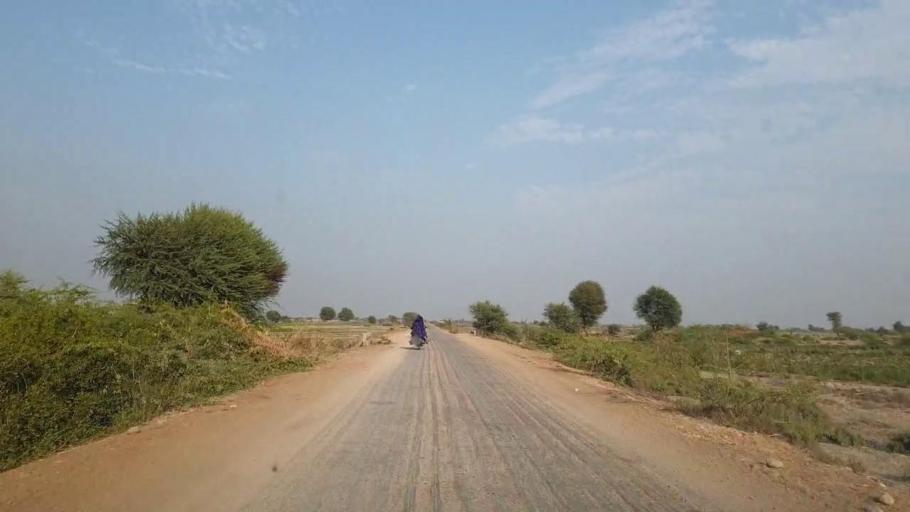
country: PK
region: Sindh
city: Pithoro
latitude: 25.5884
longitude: 69.2763
